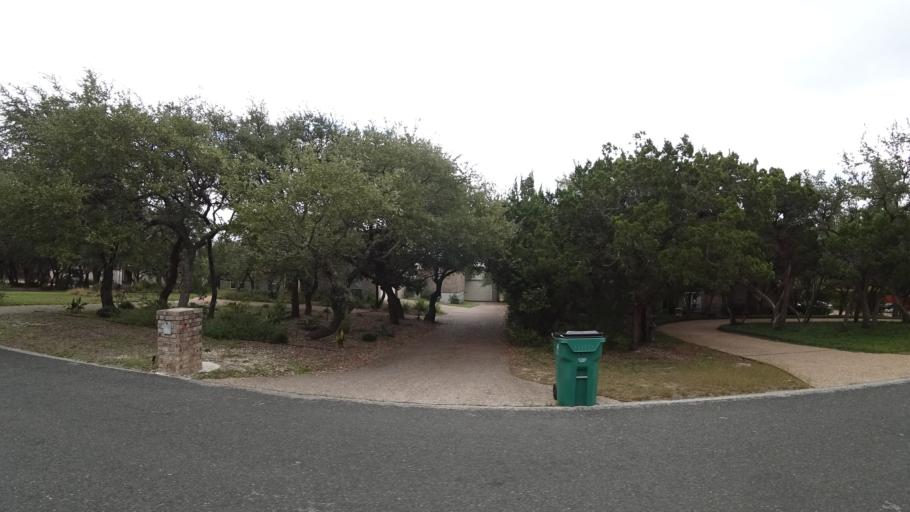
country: US
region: Texas
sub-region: Travis County
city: Barton Creek
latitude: 30.2497
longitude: -97.9110
